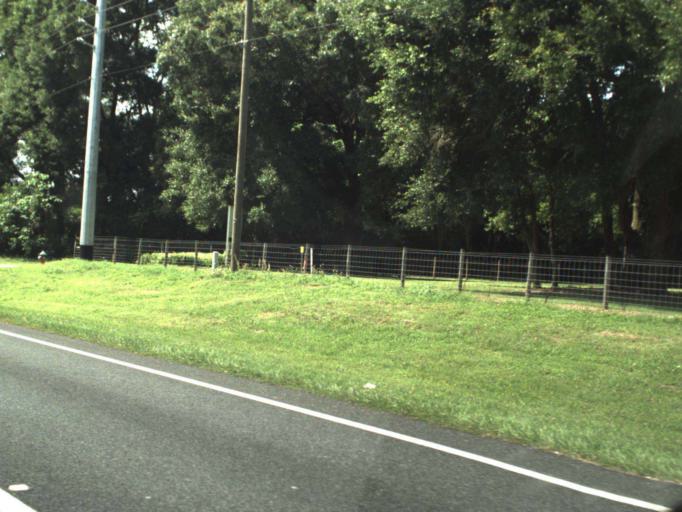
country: US
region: Florida
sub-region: Marion County
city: Silver Springs Shores
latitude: 29.1409
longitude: -82.0573
